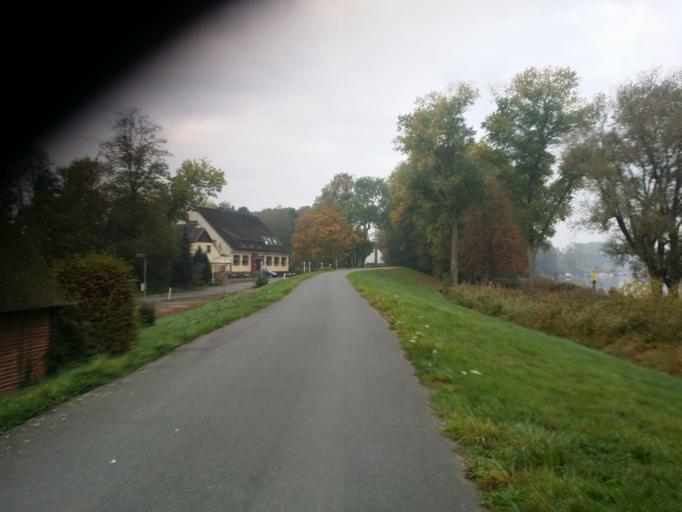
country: DE
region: Lower Saxony
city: Lemwerder
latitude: 53.1584
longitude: 8.6635
